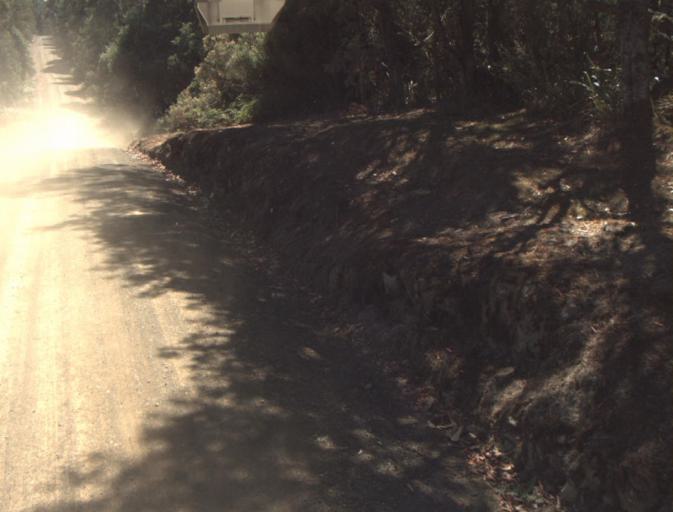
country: AU
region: Tasmania
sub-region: Dorset
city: Scottsdale
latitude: -41.2787
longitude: 147.3418
